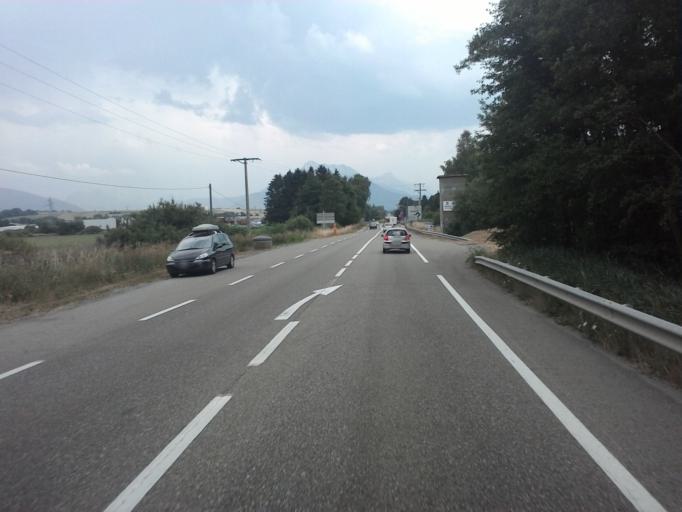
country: FR
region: Rhone-Alpes
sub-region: Departement de l'Isere
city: Pierre-Chatel
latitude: 44.9366
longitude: 5.7811
